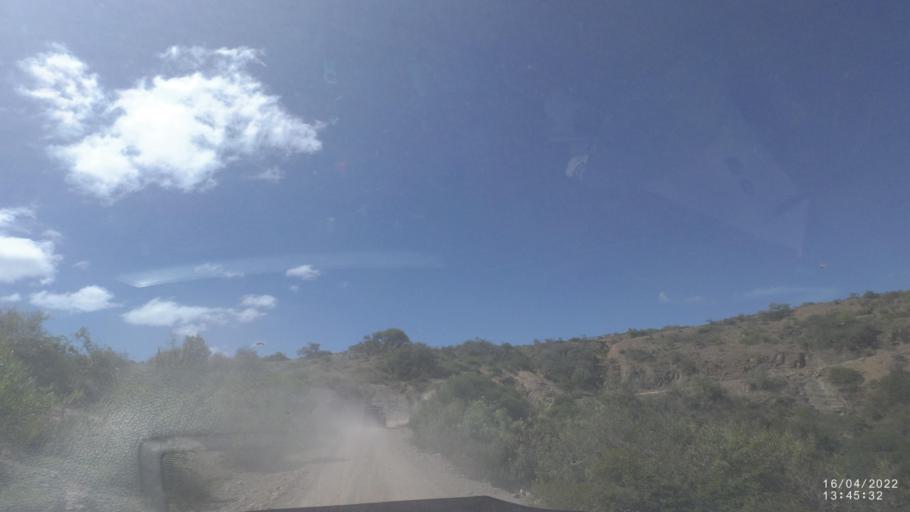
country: BO
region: Cochabamba
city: Mizque
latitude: -18.0033
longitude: -65.5911
